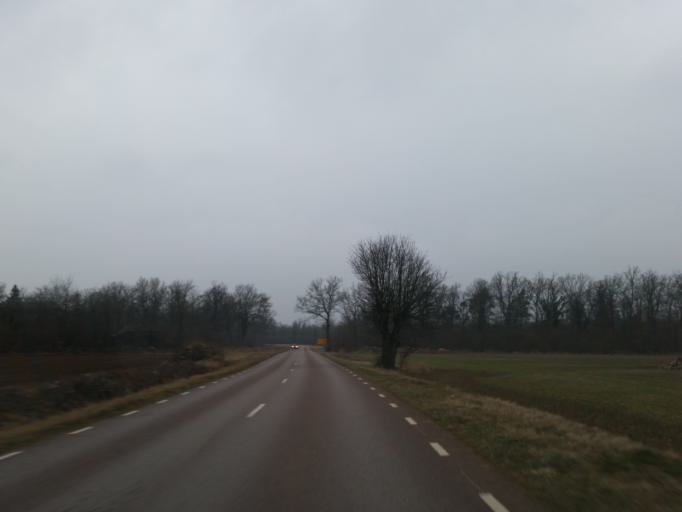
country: SE
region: Kalmar
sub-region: Morbylanga Kommun
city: Sodra Sandby
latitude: 56.6335
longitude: 16.5916
